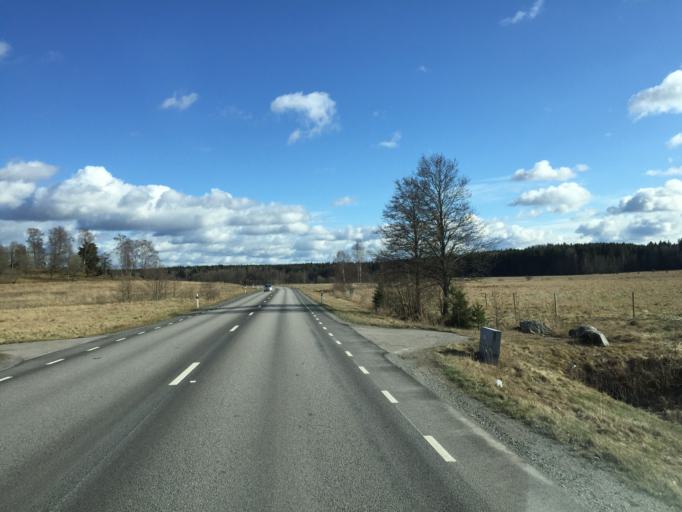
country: SE
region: Stockholm
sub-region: Sodertalje Kommun
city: Soedertaelje
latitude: 59.2256
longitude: 17.5625
